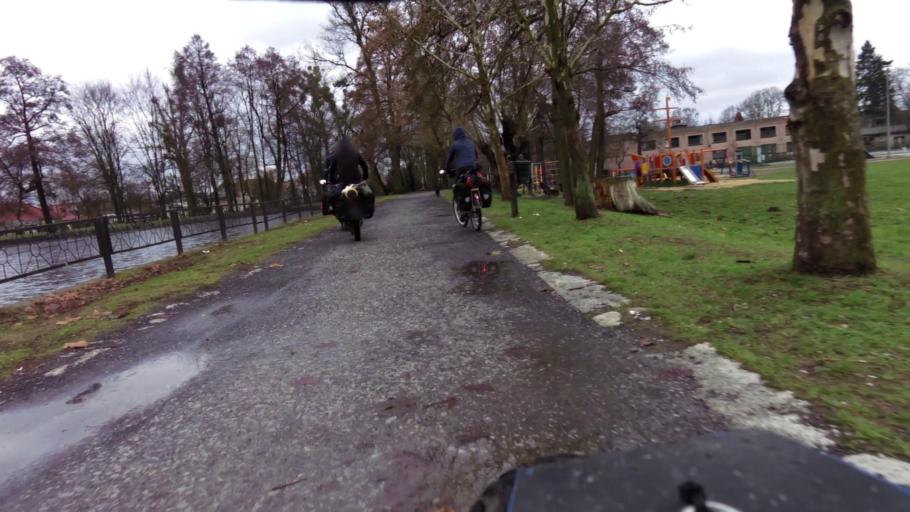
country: PL
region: Lubusz
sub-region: Powiat gorzowski
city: Witnica
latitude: 52.6761
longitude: 14.8961
